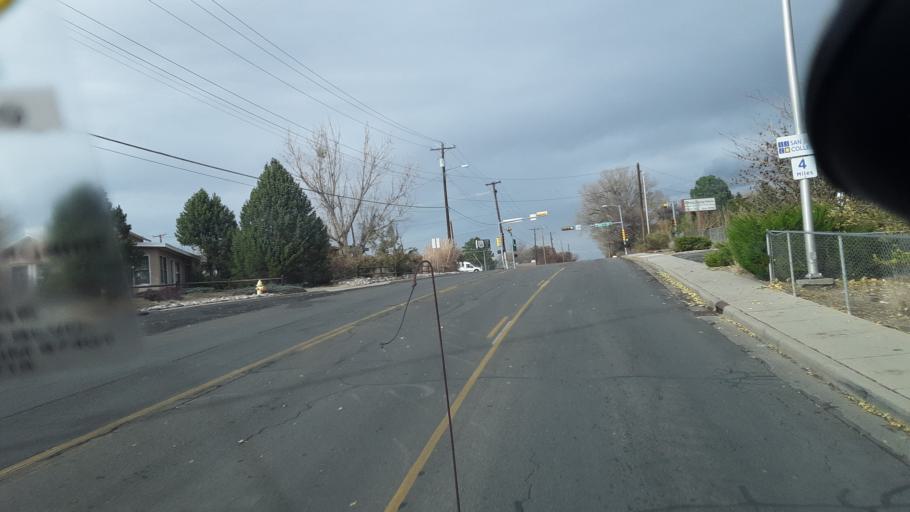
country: US
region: New Mexico
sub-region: San Juan County
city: Farmington
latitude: 36.7329
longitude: -108.1980
